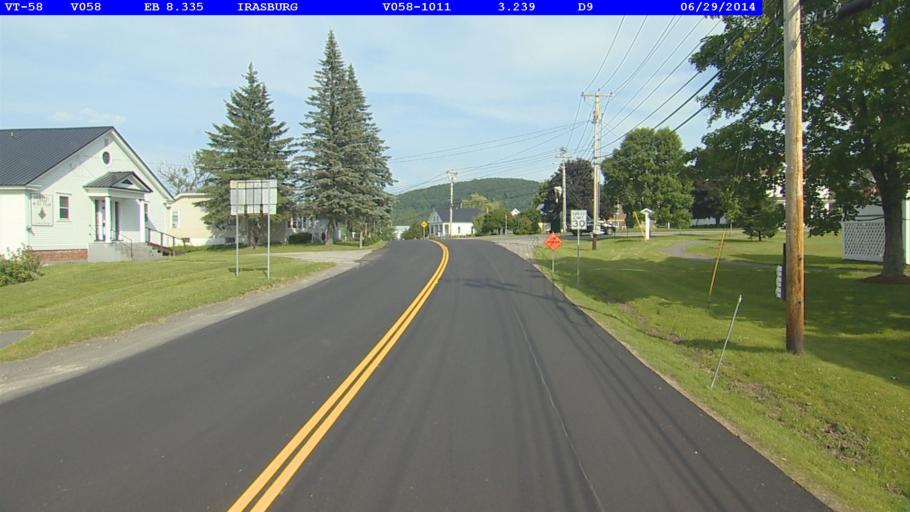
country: US
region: Vermont
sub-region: Orleans County
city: Newport
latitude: 44.8033
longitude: -72.2791
